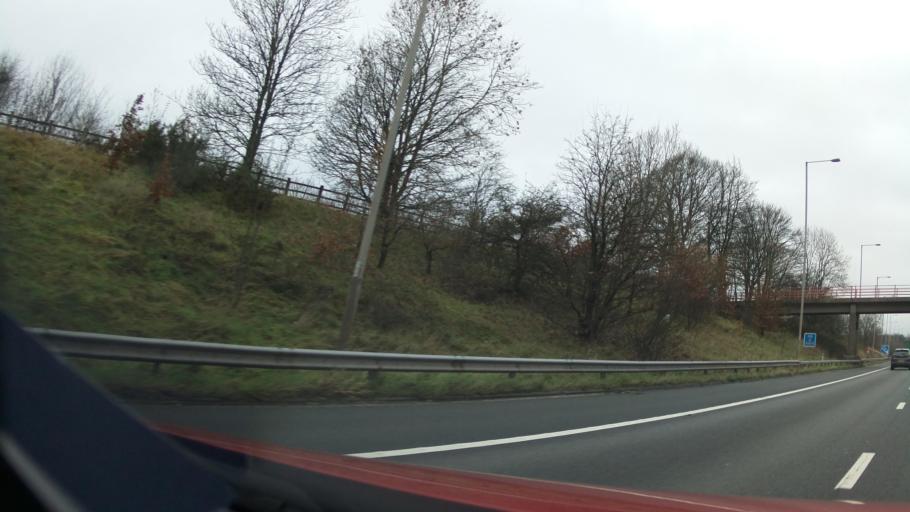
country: GB
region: England
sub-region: Lancashire
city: Euxton
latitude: 53.6752
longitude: -2.6850
